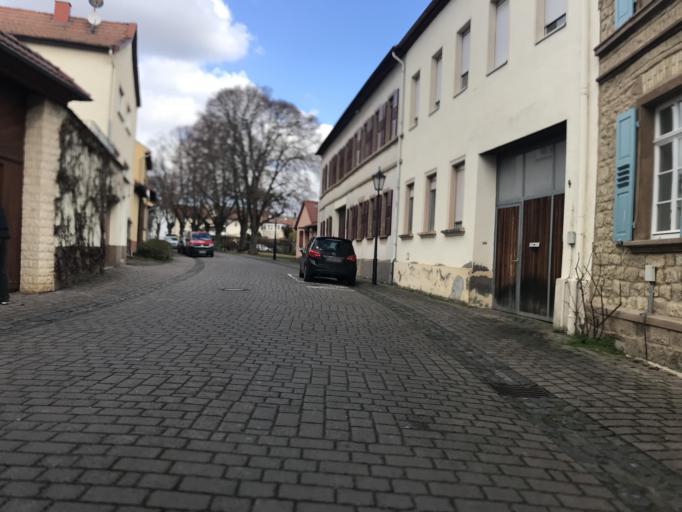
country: DE
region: Rheinland-Pfalz
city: Sankt Johann
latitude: 49.8675
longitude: 8.0181
